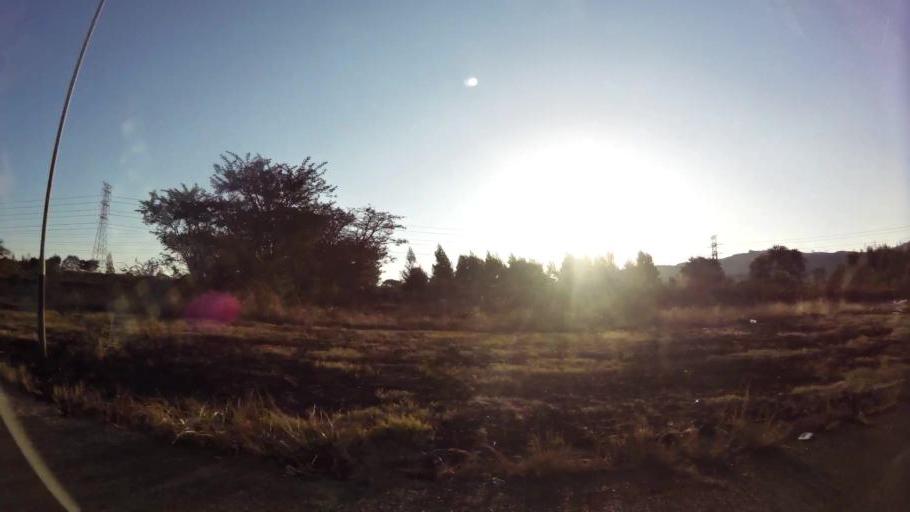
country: ZA
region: Gauteng
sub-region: City of Tshwane Metropolitan Municipality
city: Pretoria
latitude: -25.7384
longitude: 28.1071
